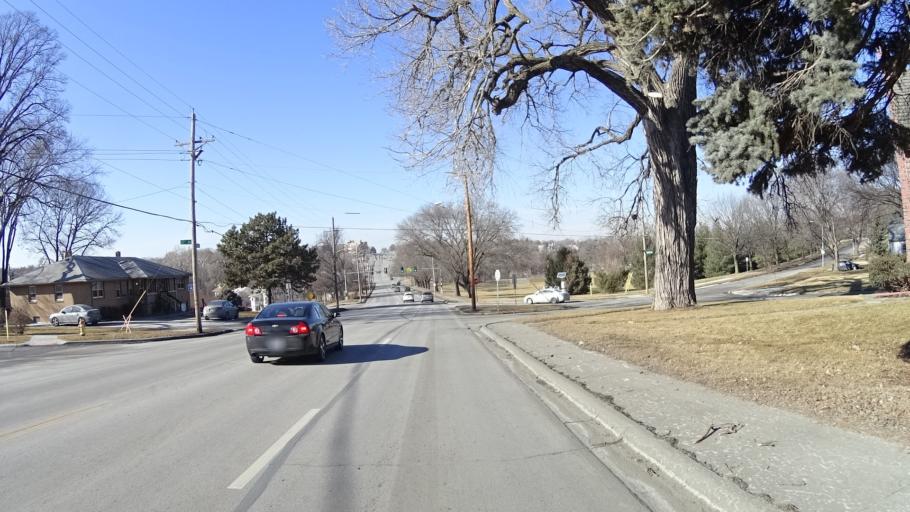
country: US
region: Nebraska
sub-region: Douglas County
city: Omaha
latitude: 41.2937
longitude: -96.0164
